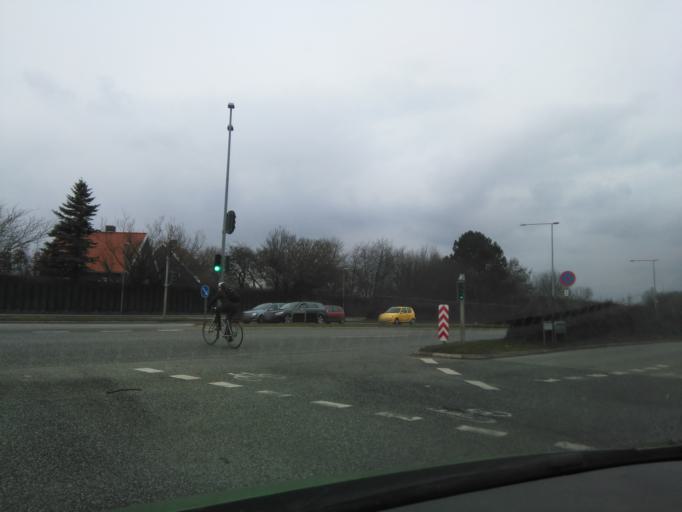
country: DK
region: Central Jutland
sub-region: Arhus Kommune
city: Arhus
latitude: 56.1781
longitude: 10.1836
